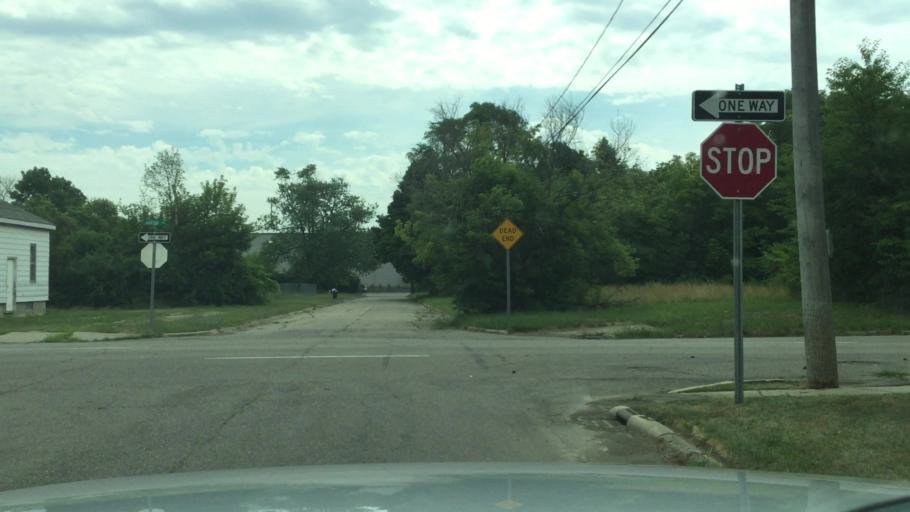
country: US
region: Michigan
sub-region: Genesee County
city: Beecher
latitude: 43.0598
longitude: -83.6827
